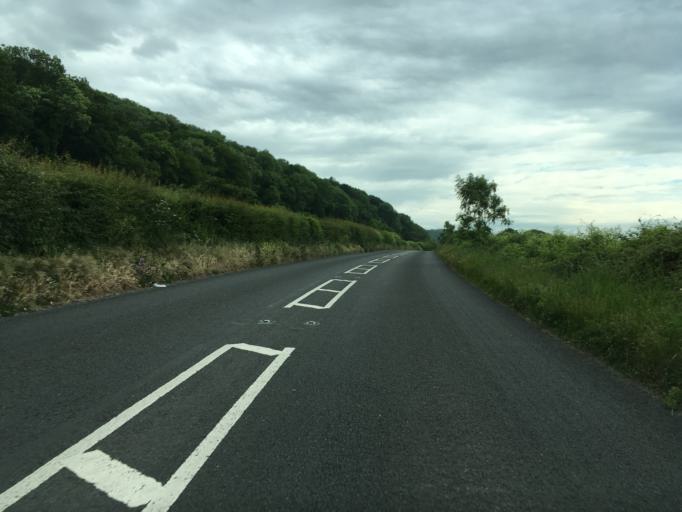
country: GB
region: England
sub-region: North Somerset
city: Clevedon
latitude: 51.4566
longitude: -2.8237
